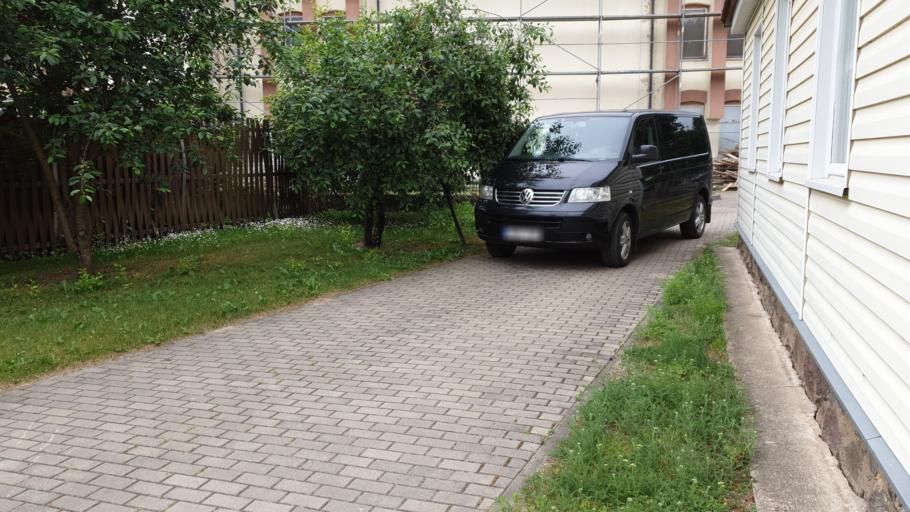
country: LT
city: Svencionys
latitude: 55.1352
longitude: 26.1603
